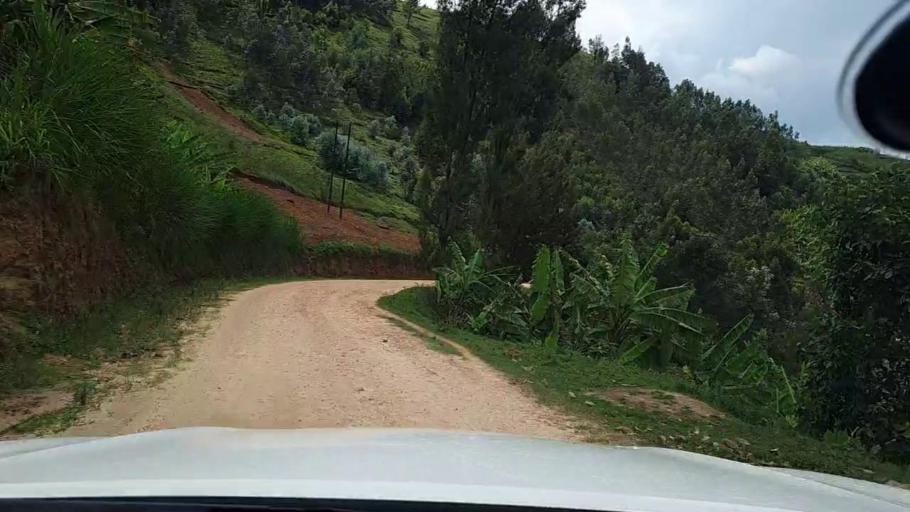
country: RW
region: Western Province
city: Kibuye
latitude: -2.1235
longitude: 29.4259
